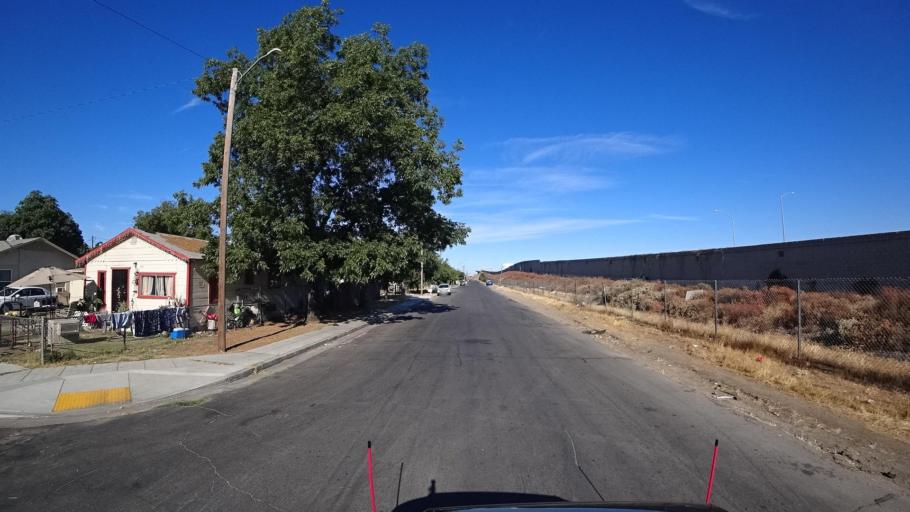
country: US
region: California
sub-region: Fresno County
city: Fresno
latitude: 36.7541
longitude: -119.7647
